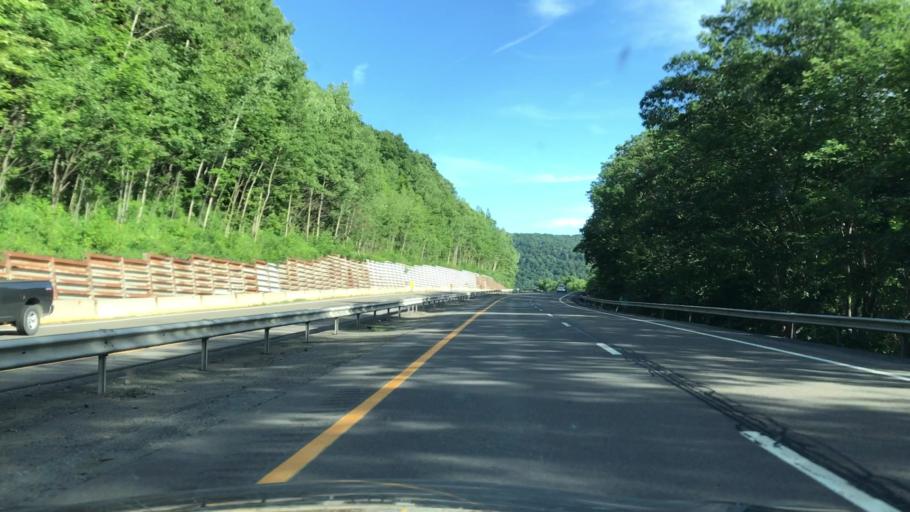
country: US
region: New York
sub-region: Broome County
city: Deposit
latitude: 42.0167
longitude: -75.4014
